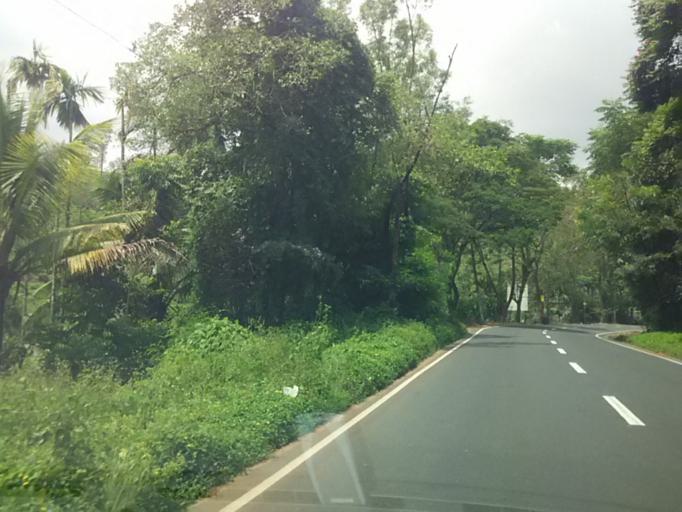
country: IN
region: Kerala
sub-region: Wayanad
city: Kalpetta
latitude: 11.5698
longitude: 76.0439
